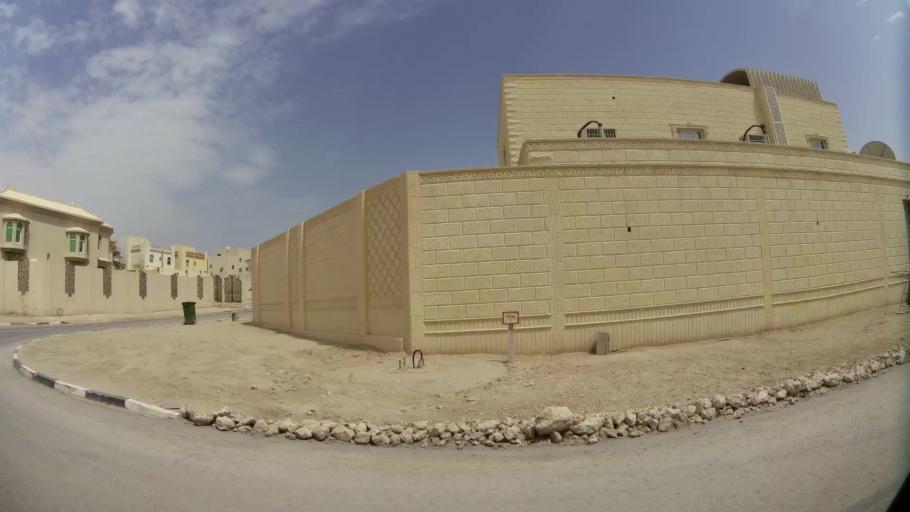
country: QA
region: Baladiyat ar Rayyan
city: Ar Rayyan
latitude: 25.3555
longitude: 51.4716
